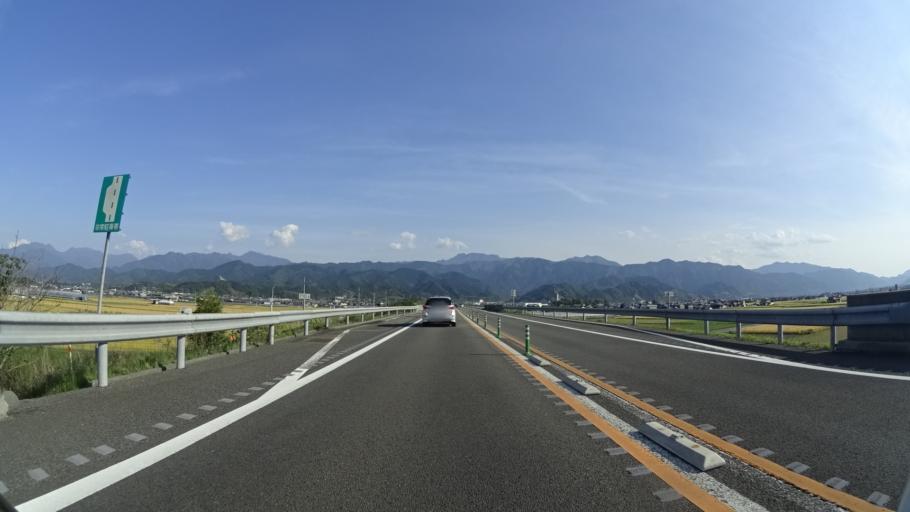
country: JP
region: Ehime
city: Saijo
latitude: 33.9063
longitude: 133.0746
